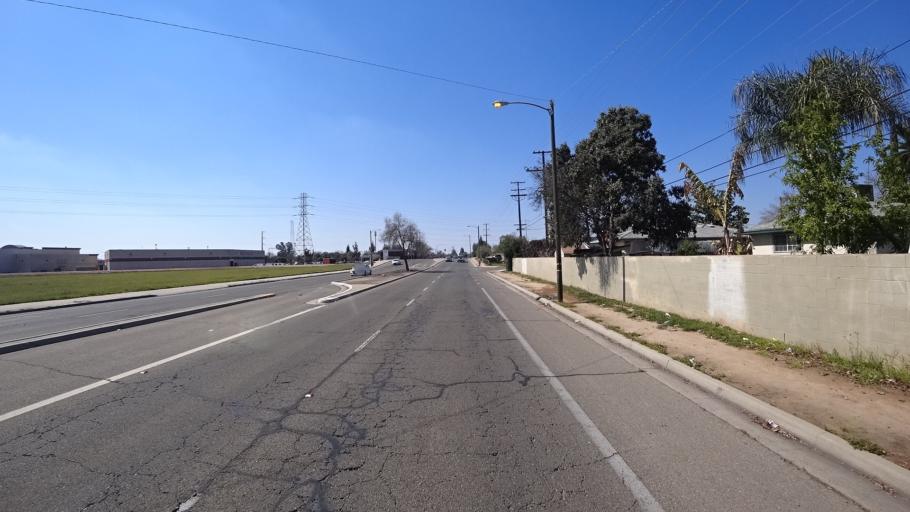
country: US
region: California
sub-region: Fresno County
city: Fresno
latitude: 36.7938
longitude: -119.8240
